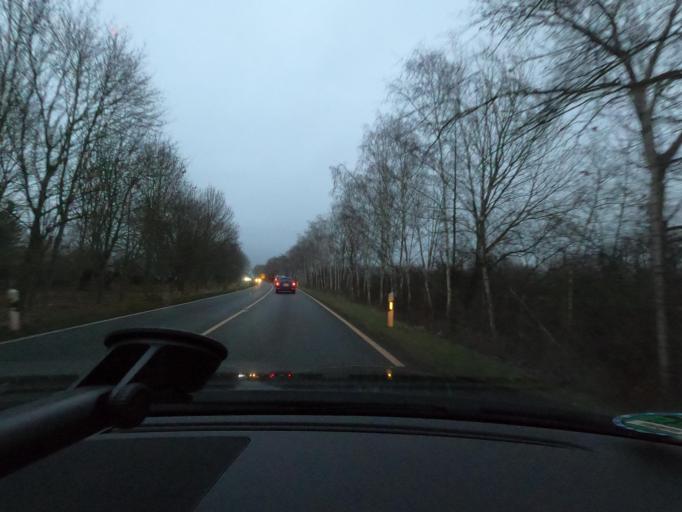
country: DE
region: Thuringia
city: Dachwig
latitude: 51.0749
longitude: 10.8583
